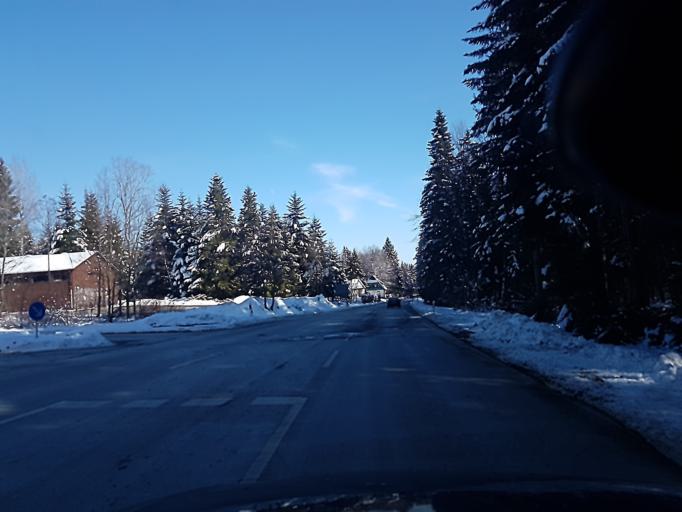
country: DE
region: Baden-Wuerttemberg
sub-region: Freiburg Region
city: Konigsfeld im Schwarzwald
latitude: 48.1358
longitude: 8.4066
